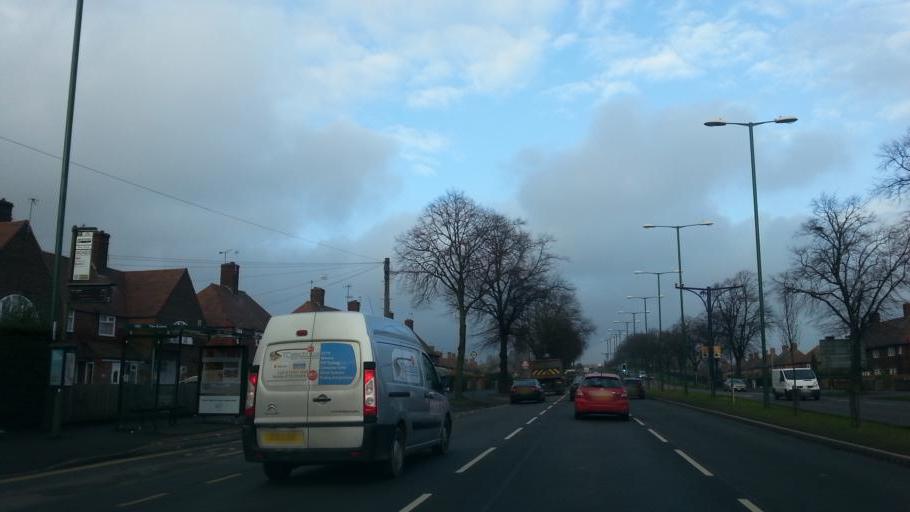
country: GB
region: England
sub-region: Nottingham
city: Nottingham
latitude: 52.9561
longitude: -1.1912
